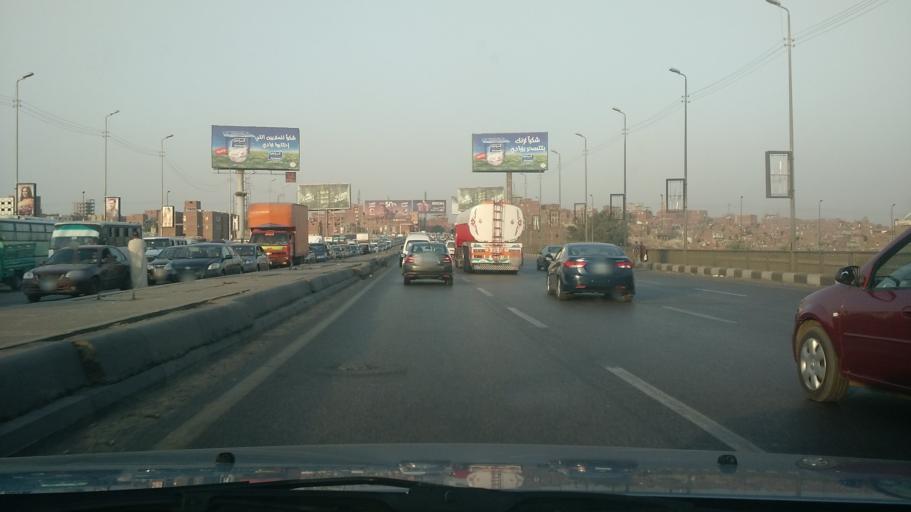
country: EG
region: Al Jizah
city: Al Jizah
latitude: 29.9909
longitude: 31.2322
